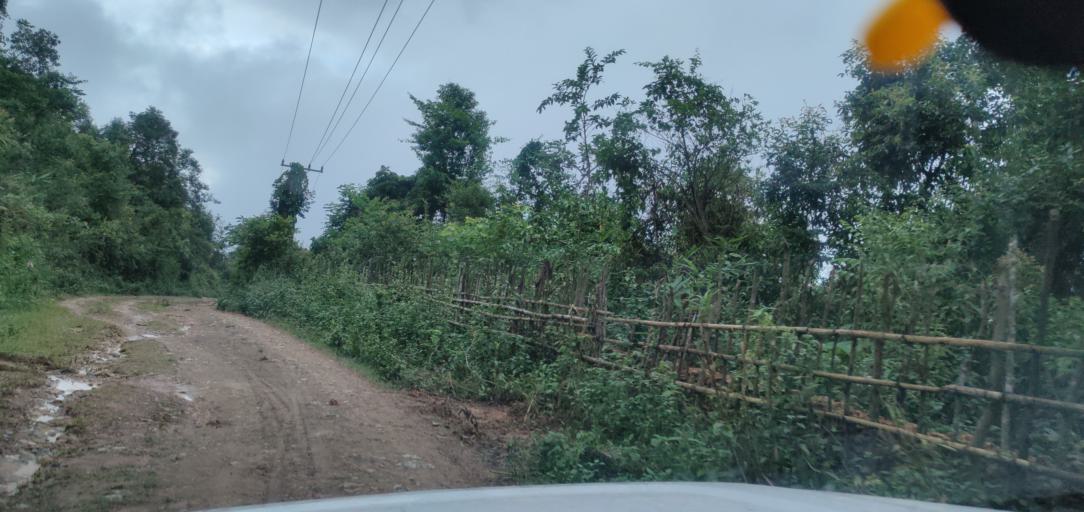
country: LA
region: Phongsali
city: Phongsali
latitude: 21.4308
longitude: 102.2615
